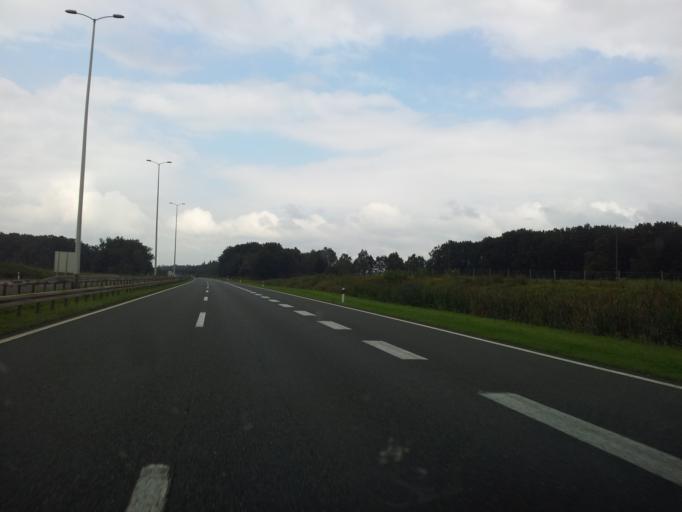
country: HR
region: Sisacko-Moslavacka
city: Lipovljani
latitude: 45.4067
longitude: 16.8570
